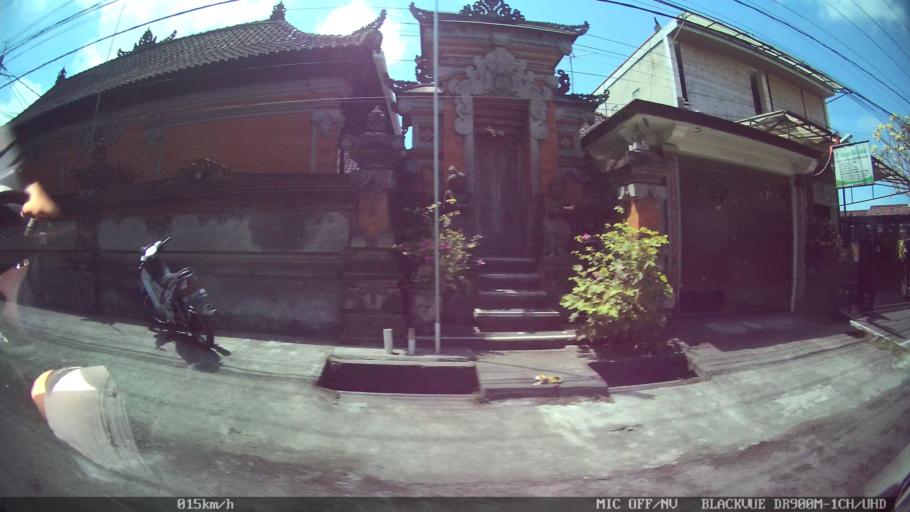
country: ID
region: Bali
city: Banjar Paangkelod
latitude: -8.6117
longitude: 115.2586
